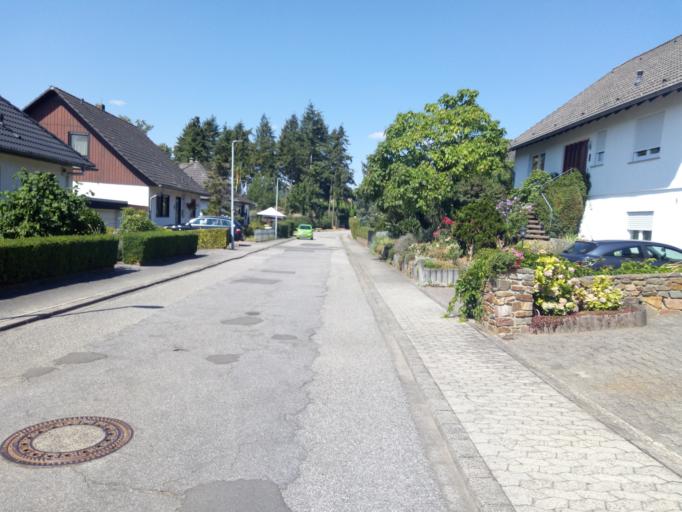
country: DE
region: Rheinland-Pfalz
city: Waldlaubersheim
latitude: 49.9294
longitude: 7.8361
